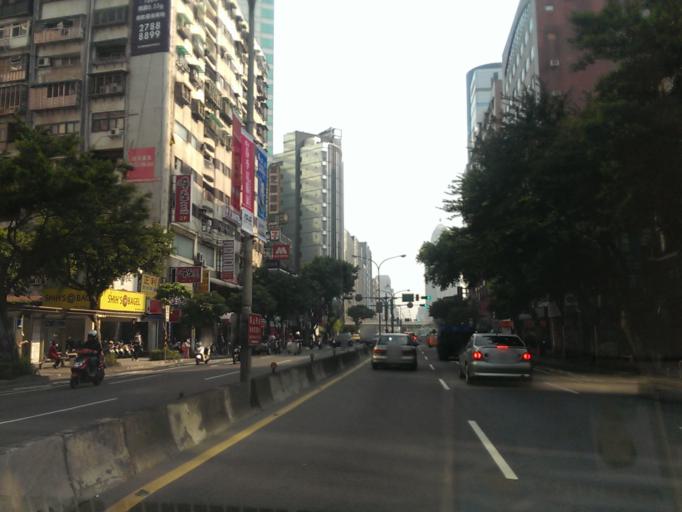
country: TW
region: Taipei
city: Taipei
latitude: 25.0313
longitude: 121.5585
